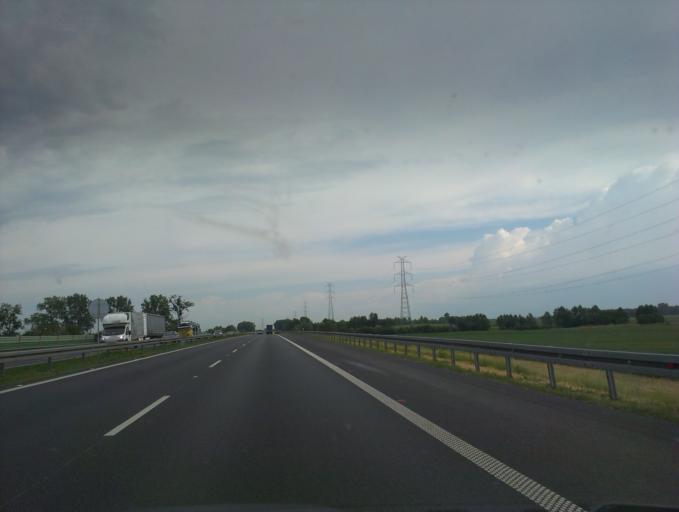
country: PL
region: Opole Voivodeship
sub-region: Powiat brzeski
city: Skarbimierz Osiedle
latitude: 50.8087
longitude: 17.3151
